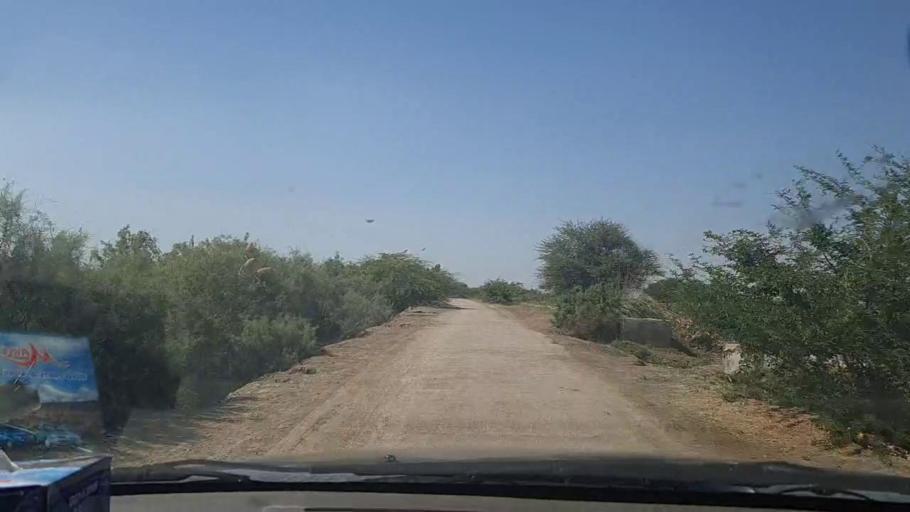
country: PK
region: Sindh
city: Chuhar Jamali
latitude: 24.2843
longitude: 67.7600
